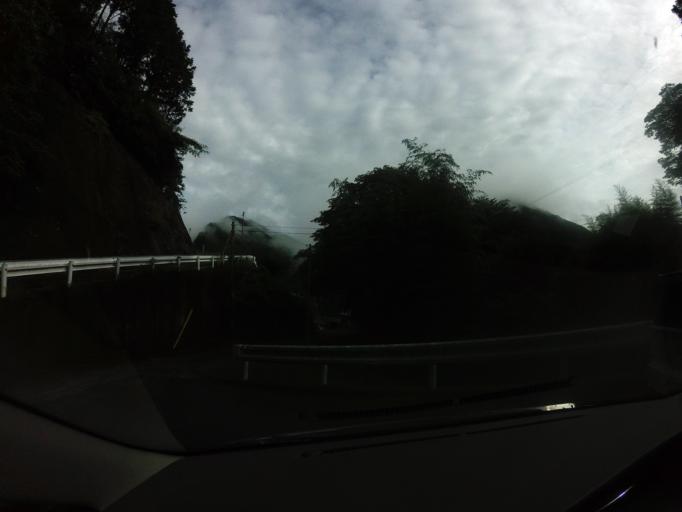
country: JP
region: Wakayama
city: Shingu
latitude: 33.9670
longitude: 135.8125
